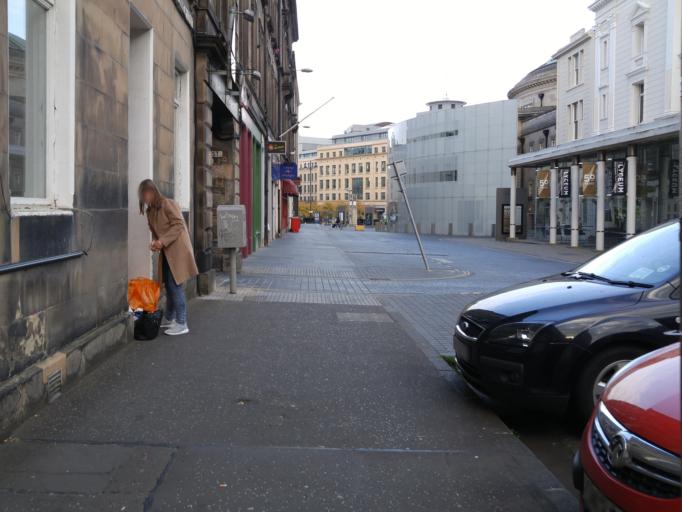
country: GB
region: Scotland
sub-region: Edinburgh
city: Edinburgh
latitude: 55.9467
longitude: -3.2041
